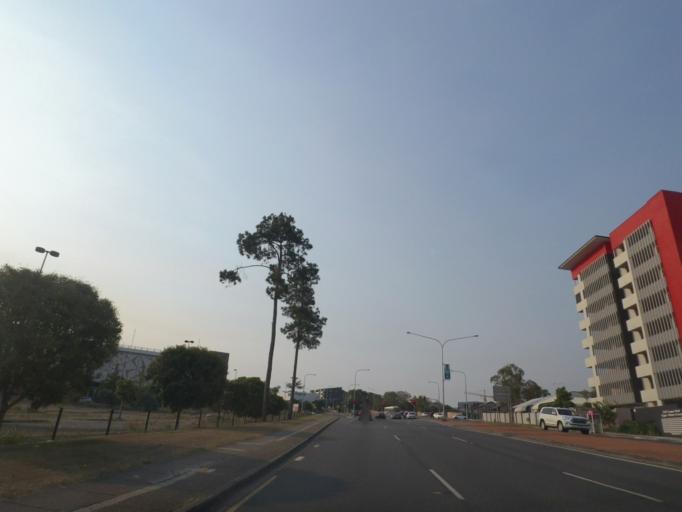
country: AU
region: Queensland
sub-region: Brisbane
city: Upper Mount Gravatt
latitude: -27.5650
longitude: 153.0872
